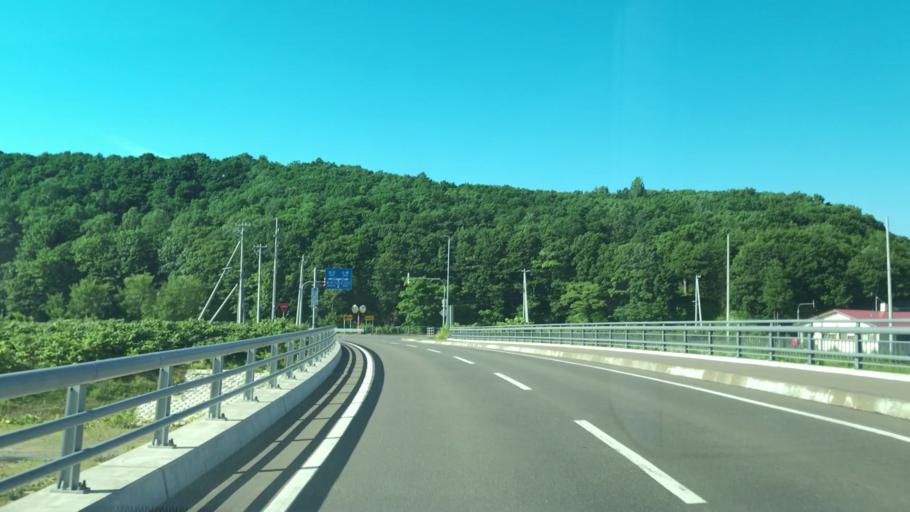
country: JP
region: Hokkaido
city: Yoichi
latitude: 43.0500
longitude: 140.8246
